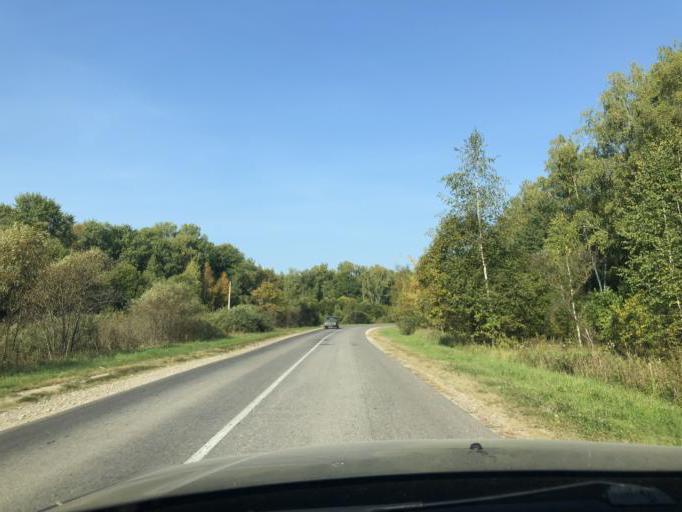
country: RU
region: Tula
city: Leninskiy
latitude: 54.3318
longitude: 37.3872
